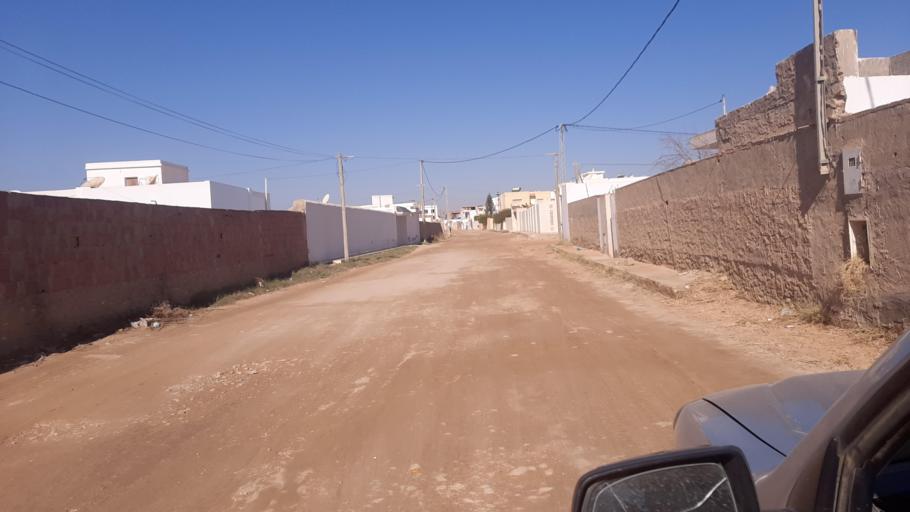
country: TN
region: Safaqis
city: Al Qarmadah
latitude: 34.7912
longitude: 10.8104
